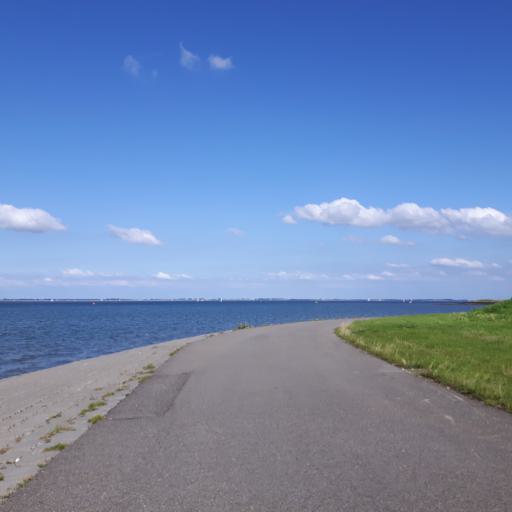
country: NL
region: Zeeland
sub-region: Gemeente Goes
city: Goes
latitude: 51.5456
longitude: 3.9124
